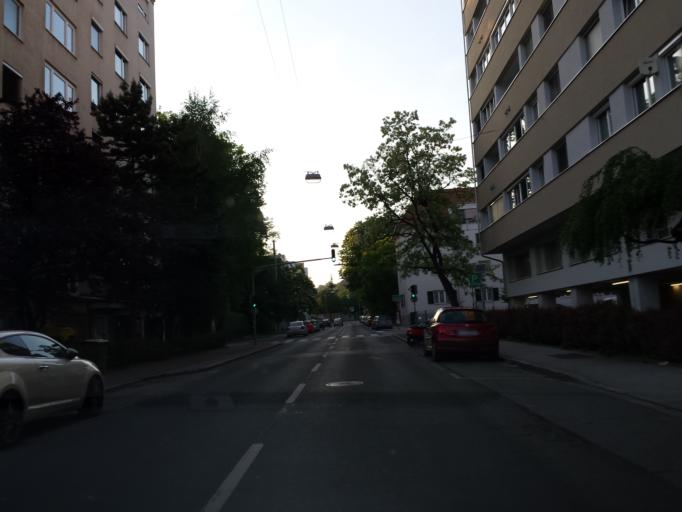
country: AT
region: Styria
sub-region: Graz Stadt
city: Graz
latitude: 47.0832
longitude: 15.4392
